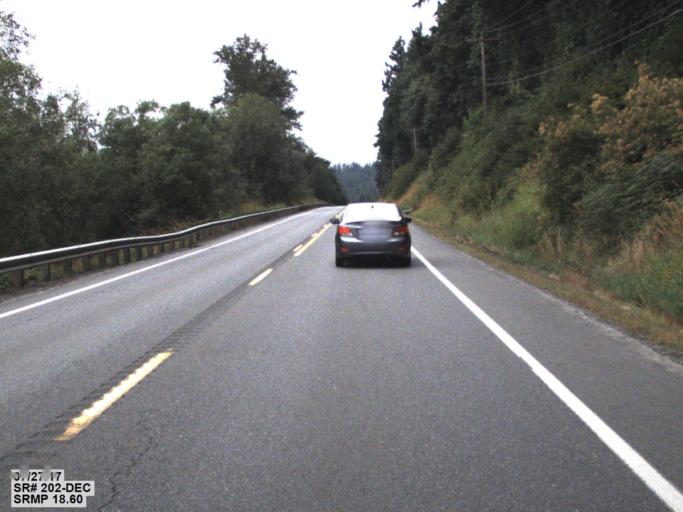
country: US
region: Washington
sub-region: King County
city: Ames Lake
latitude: 47.5850
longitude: -121.9473
